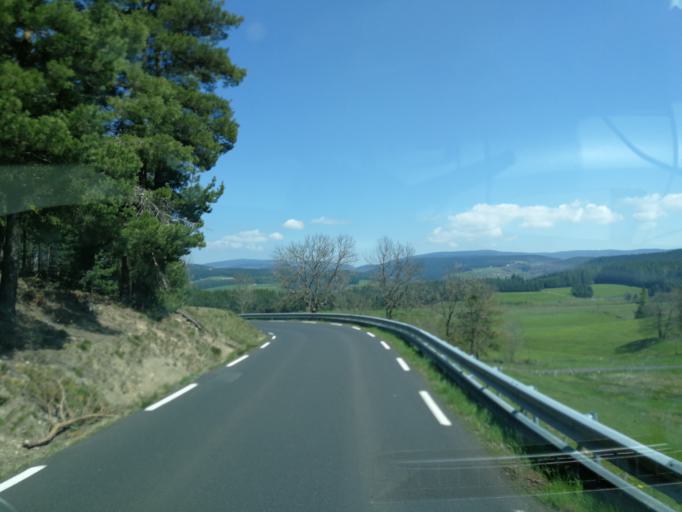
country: FR
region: Auvergne
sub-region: Departement de la Haute-Loire
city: Dunieres
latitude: 45.2002
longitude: 4.3438
